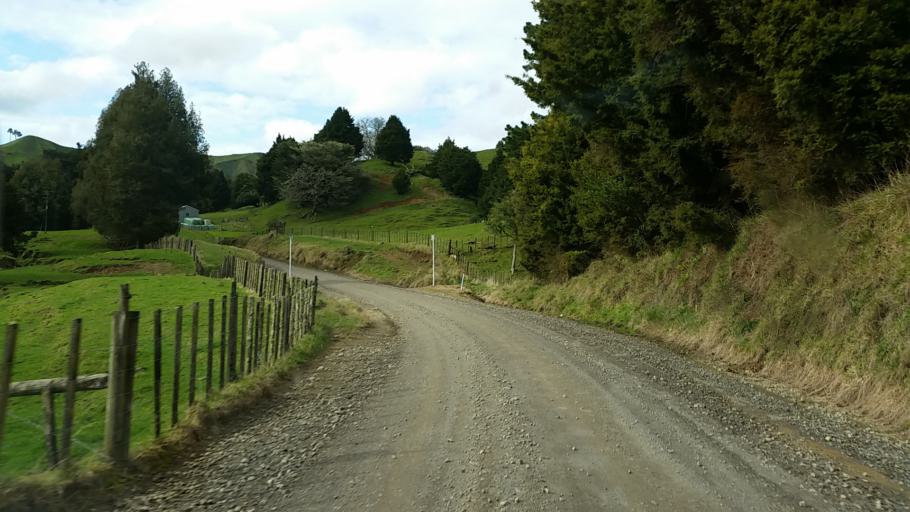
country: NZ
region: Taranaki
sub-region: New Plymouth District
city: Waitara
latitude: -39.1622
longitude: 174.5838
